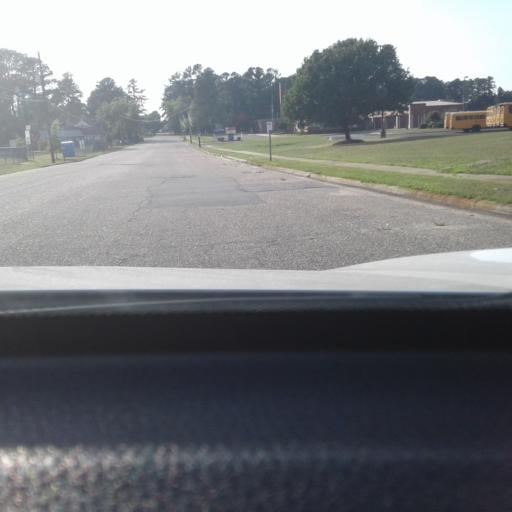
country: US
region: North Carolina
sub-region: Harnett County
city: Dunn
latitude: 35.3142
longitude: -78.6163
